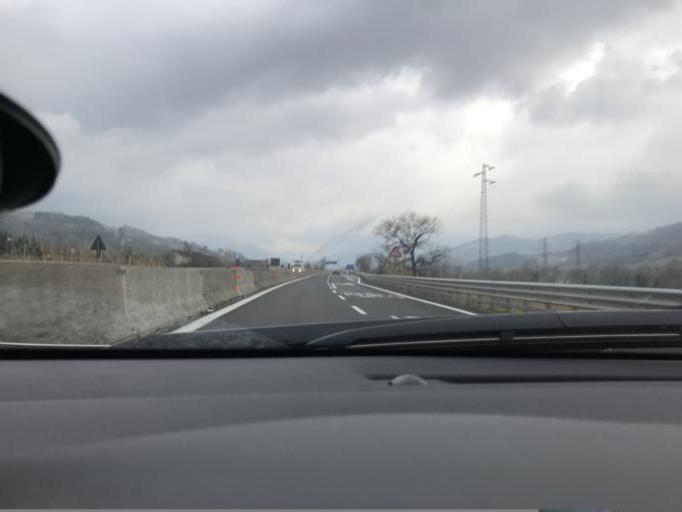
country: IT
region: The Marches
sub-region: Provincia di Ancona
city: Rosora
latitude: 43.4663
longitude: 13.0674
